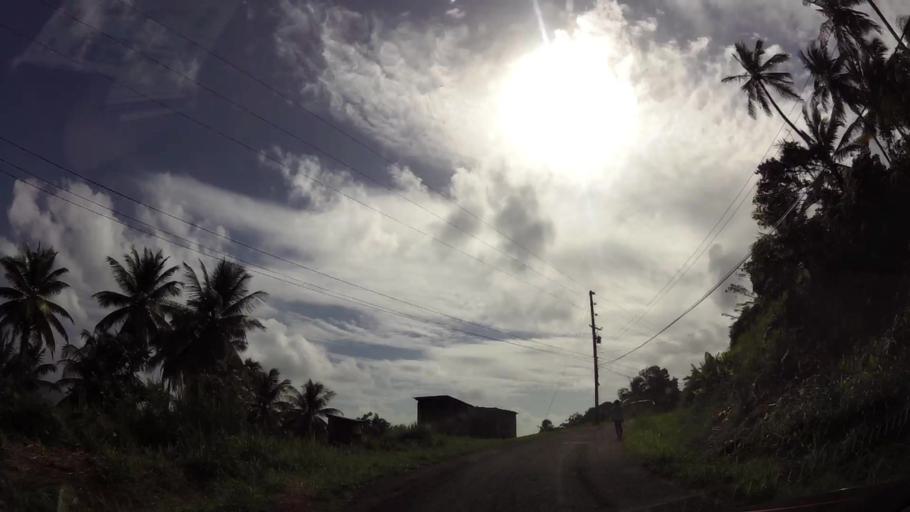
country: DM
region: Saint David
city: Castle Bruce
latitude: 15.4683
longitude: -61.2484
